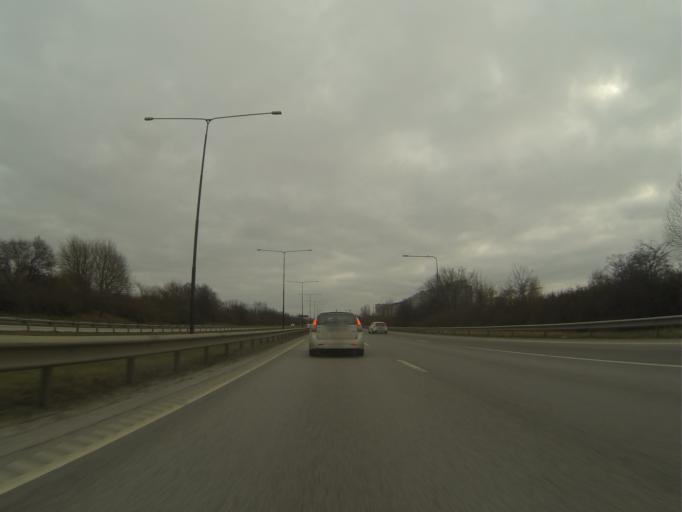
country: SE
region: Skane
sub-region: Burlovs Kommun
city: Arloev
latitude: 55.5933
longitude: 13.0538
